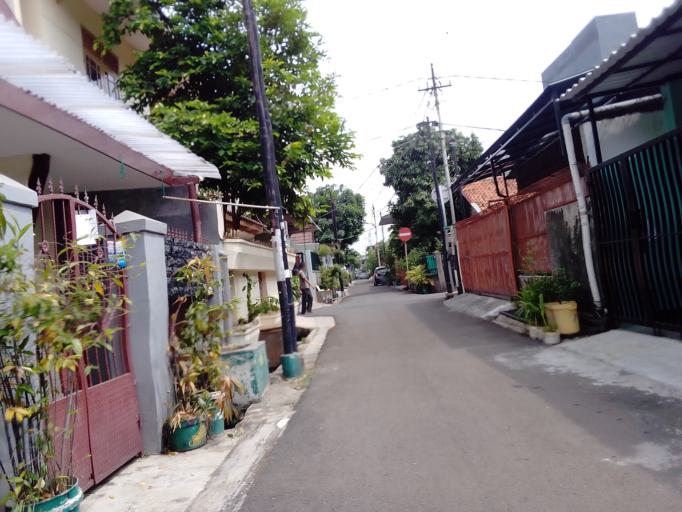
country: ID
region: Jakarta Raya
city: Jakarta
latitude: -6.1738
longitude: 106.8082
